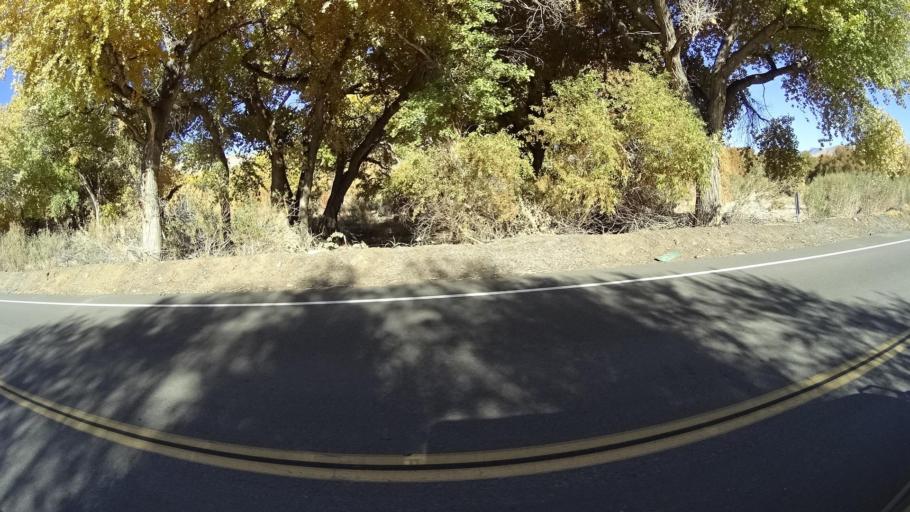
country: US
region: California
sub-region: Kern County
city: Weldon
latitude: 35.6707
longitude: -118.3245
